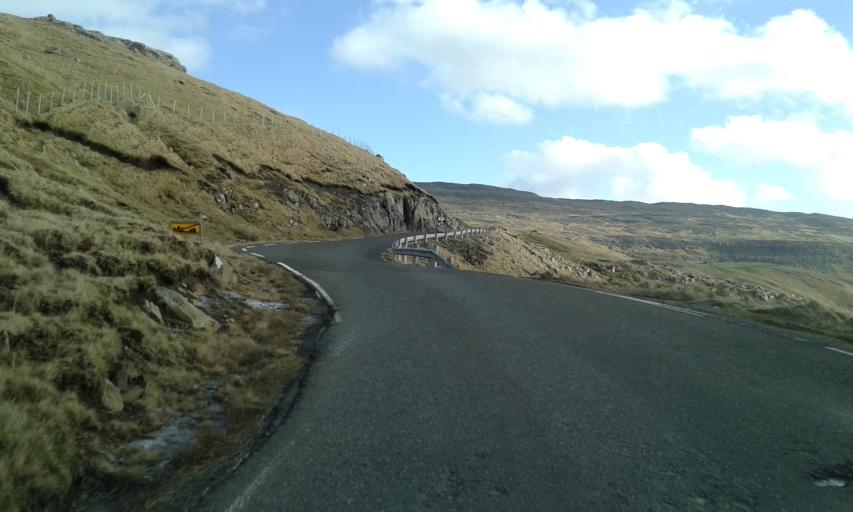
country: FO
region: Streymoy
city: Argir
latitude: 61.9835
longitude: -6.8532
